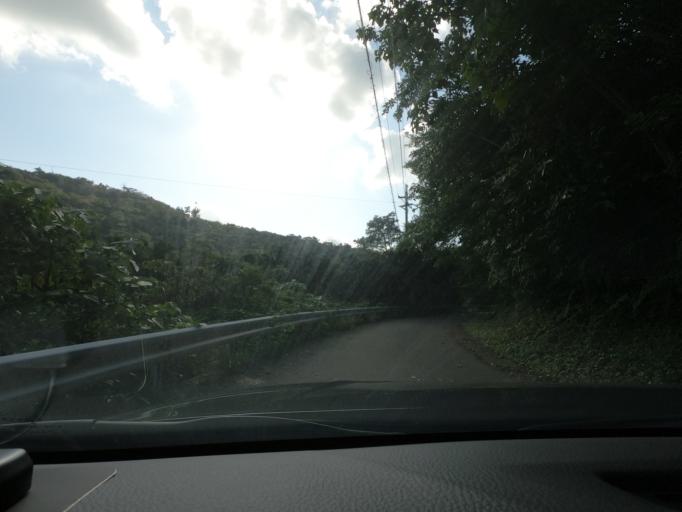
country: JP
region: Okinawa
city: Nago
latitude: 26.7641
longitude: 128.2159
